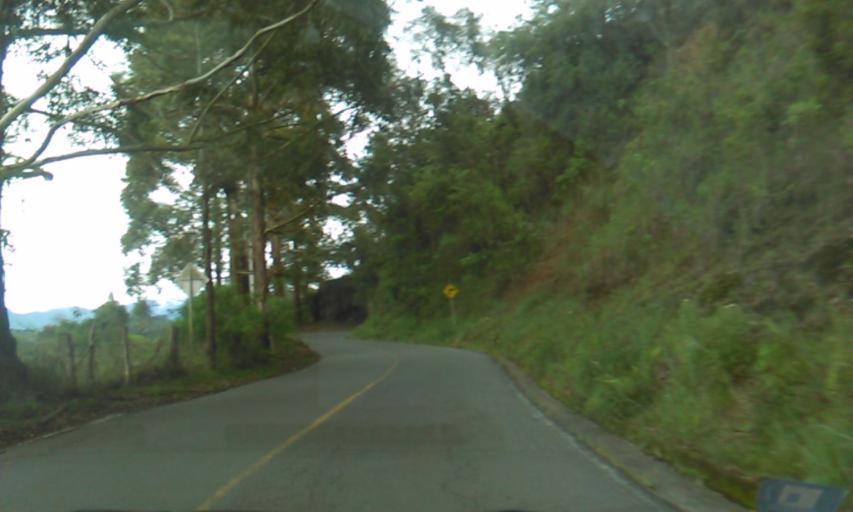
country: CO
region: Quindio
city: Salento
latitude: 4.6432
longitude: -75.5732
